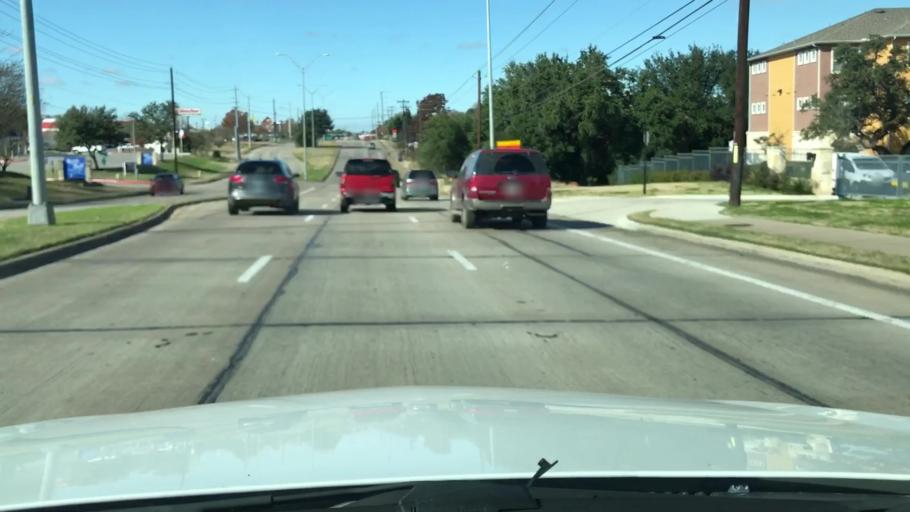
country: US
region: Texas
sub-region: Travis County
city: Onion Creek
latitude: 30.1875
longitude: -97.7619
